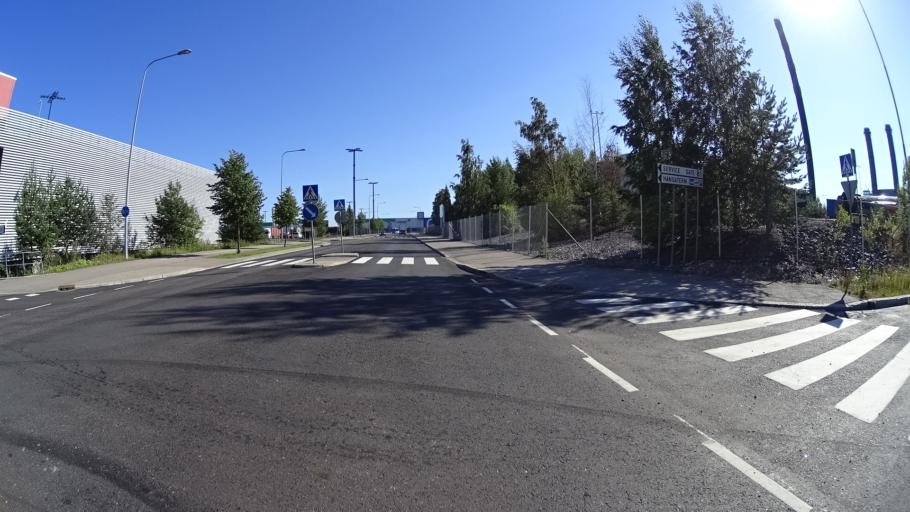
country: FI
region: Uusimaa
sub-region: Helsinki
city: Vantaa
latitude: 60.2217
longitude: 25.1734
